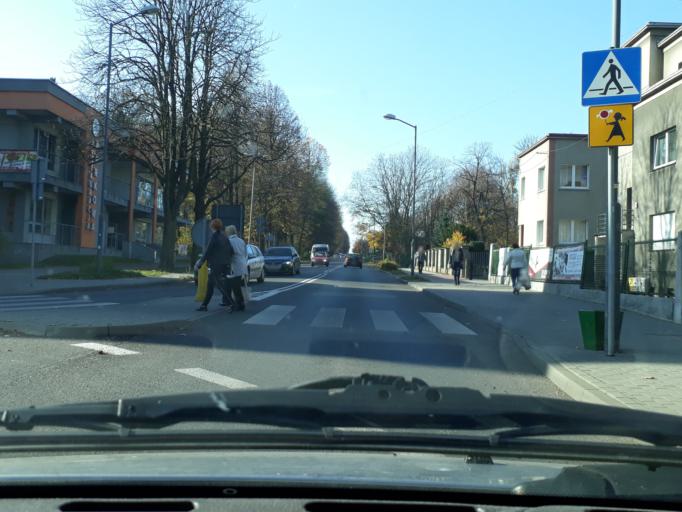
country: PL
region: Silesian Voivodeship
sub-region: Powiat tarnogorski
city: Tarnowskie Gory
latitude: 50.4423
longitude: 18.8513
